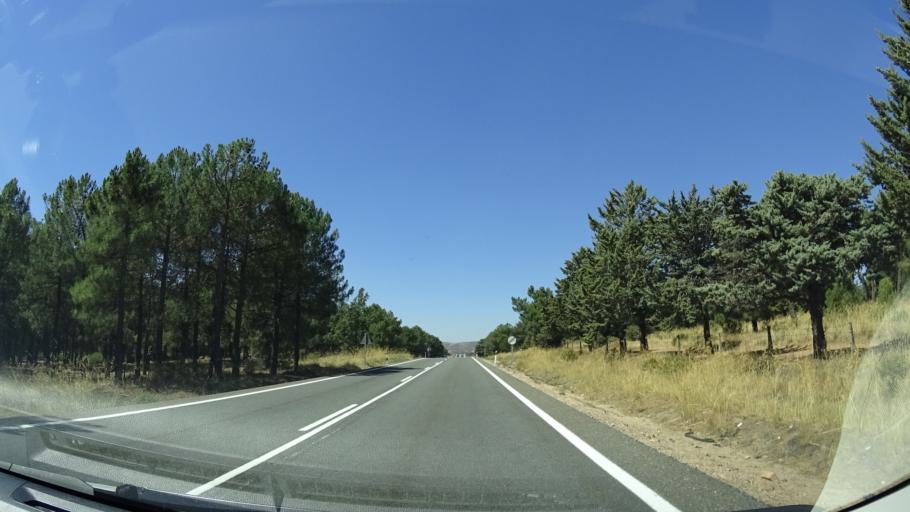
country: ES
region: Castille and Leon
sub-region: Provincia de Avila
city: Navalperal de Pinares
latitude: 40.5872
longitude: -4.4013
